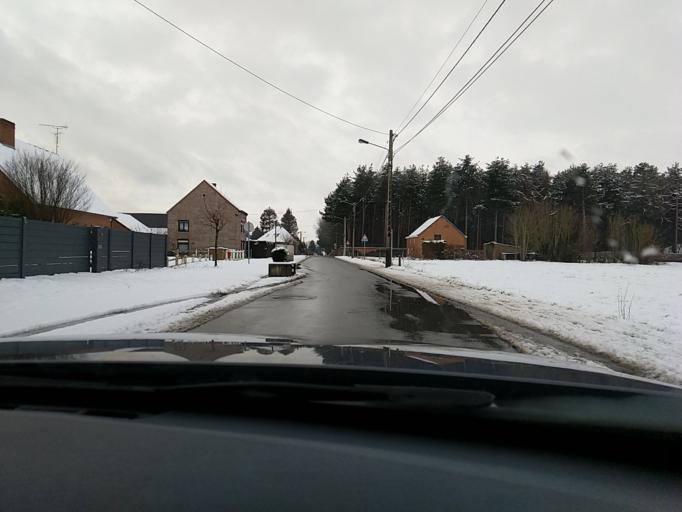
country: BE
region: Wallonia
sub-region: Province du Hainaut
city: Jurbise
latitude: 50.5097
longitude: 3.9350
